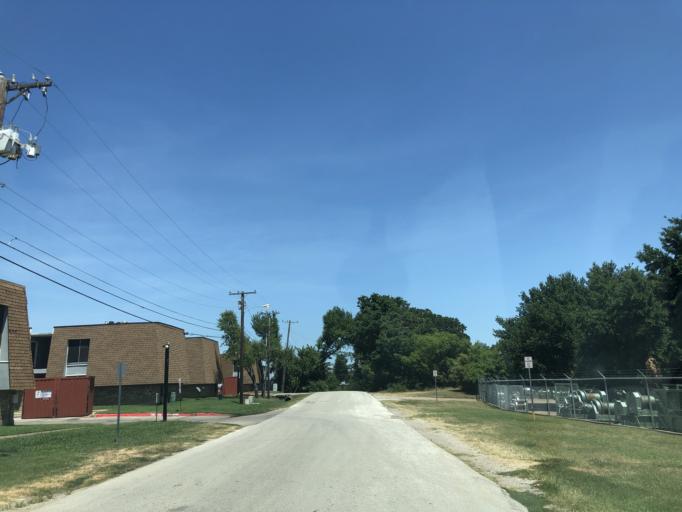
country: US
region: Texas
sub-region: Dallas County
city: Irving
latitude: 32.8298
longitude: -96.9041
